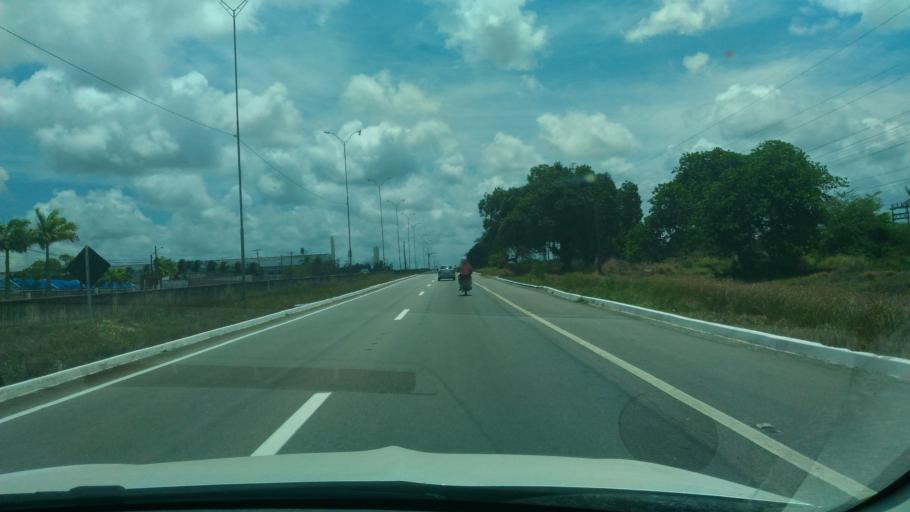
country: BR
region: Paraiba
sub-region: Conde
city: Conde
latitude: -7.2456
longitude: -34.9308
